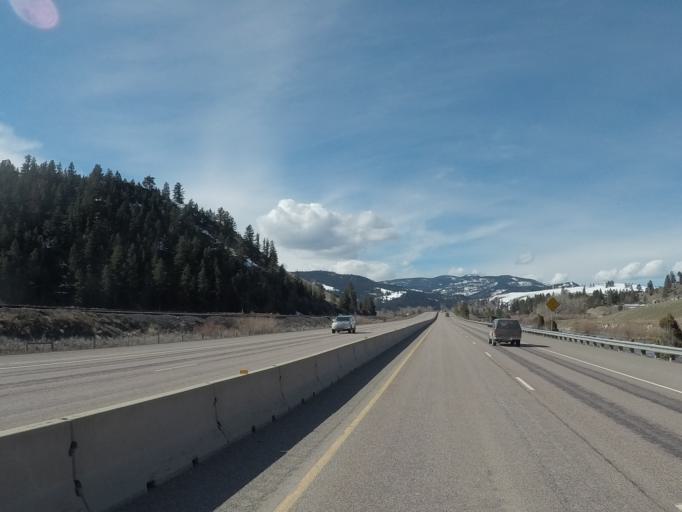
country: US
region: Montana
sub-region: Granite County
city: Philipsburg
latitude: 46.7154
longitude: -113.3239
